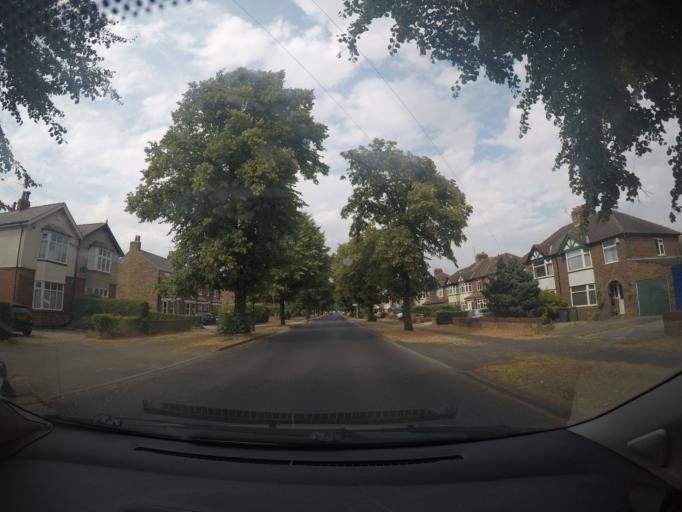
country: GB
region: England
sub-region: City of York
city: Nether Poppleton
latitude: 53.9595
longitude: -1.1351
